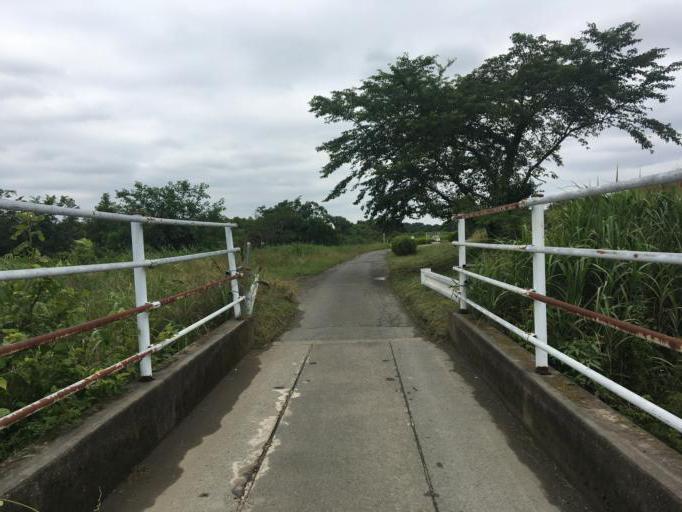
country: JP
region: Saitama
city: Okegawa
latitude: 35.9473
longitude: 139.5455
